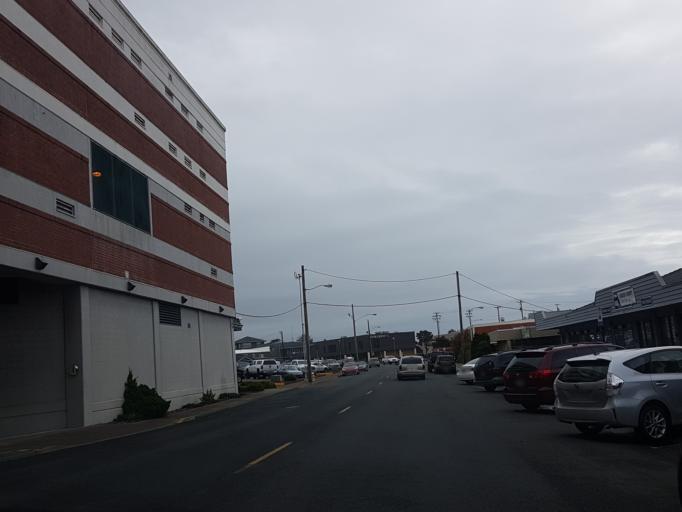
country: US
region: Oregon
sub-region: Lincoln County
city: Newport
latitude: 44.6363
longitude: -124.0557
